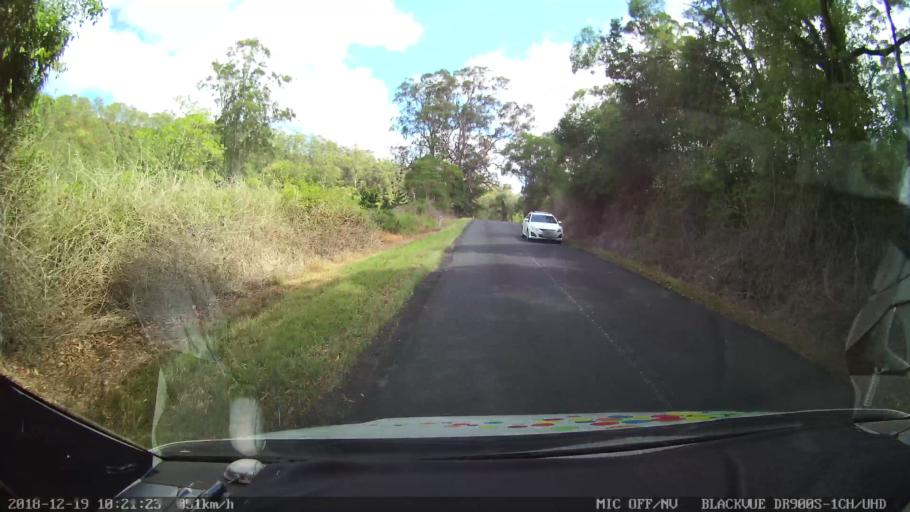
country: AU
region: New South Wales
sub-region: Kyogle
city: Kyogle
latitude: -28.5985
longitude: 153.0596
